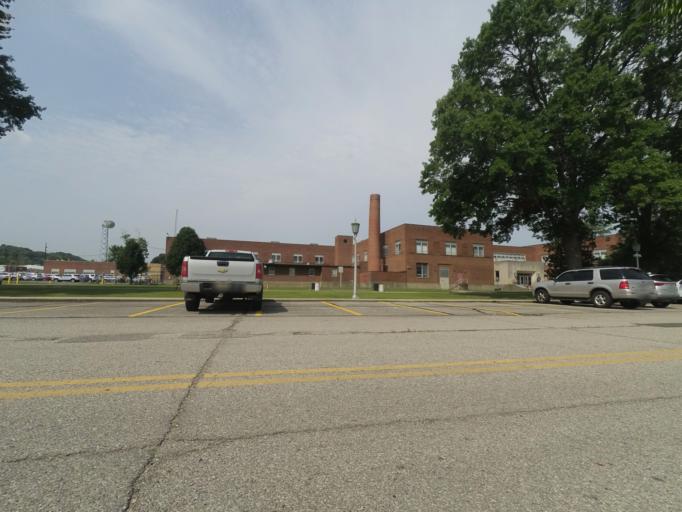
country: US
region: West Virginia
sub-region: Cabell County
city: Huntington
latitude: 38.4110
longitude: -82.4670
